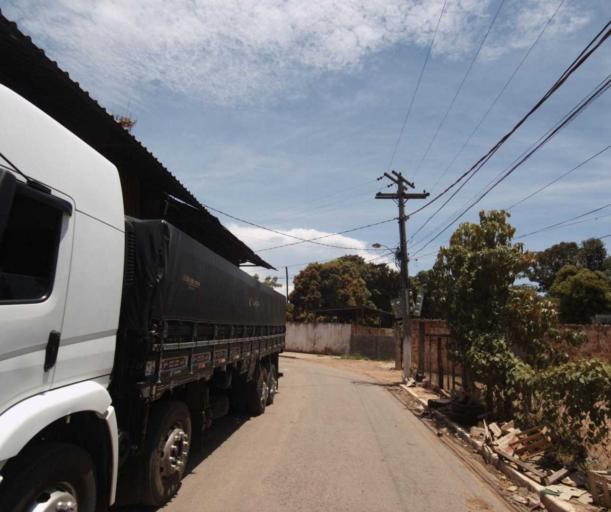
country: BR
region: Mato Grosso
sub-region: Cuiaba
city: Cuiaba
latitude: -15.6060
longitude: -56.1270
